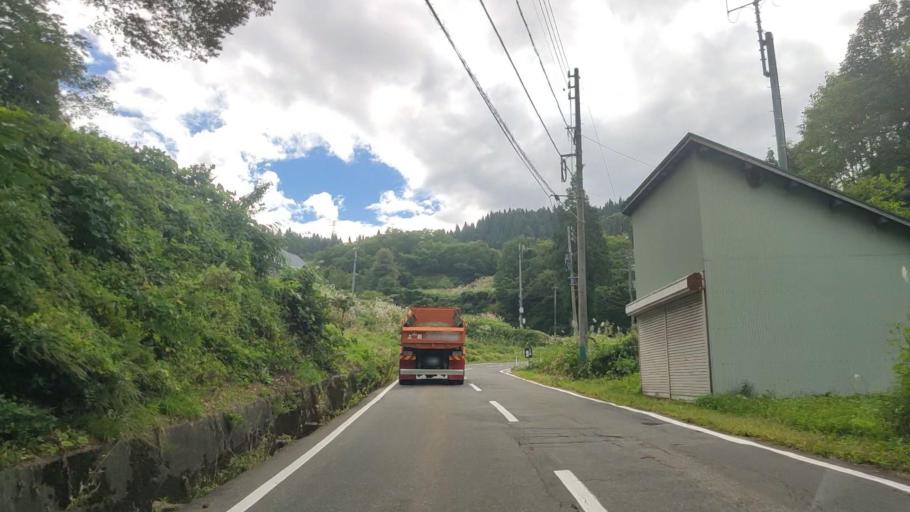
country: JP
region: Nagano
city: Iiyama
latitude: 36.8818
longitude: 138.3205
